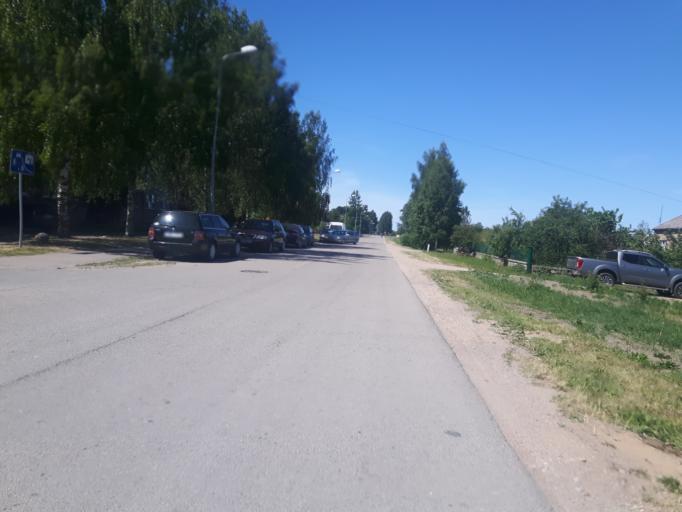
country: LV
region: Grobina
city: Grobina
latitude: 56.5363
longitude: 21.1776
